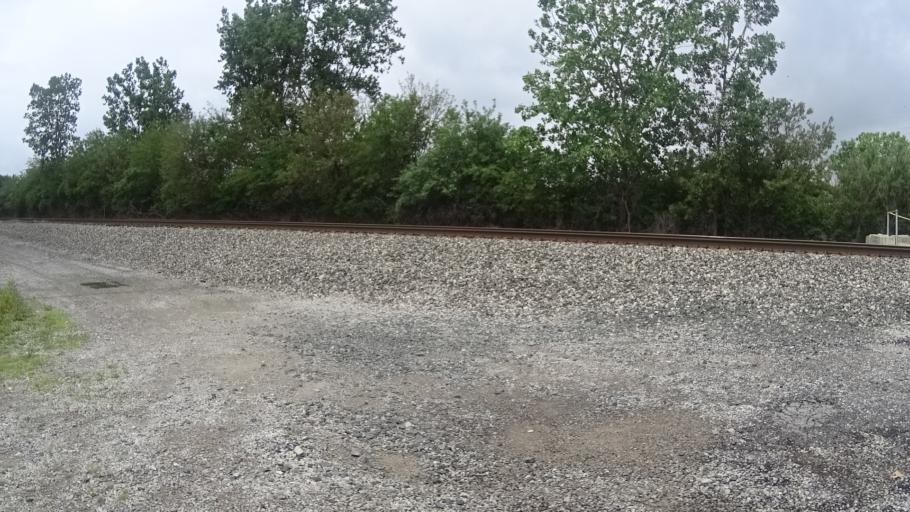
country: US
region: Ohio
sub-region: Huron County
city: Bellevue
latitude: 41.3462
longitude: -82.7855
